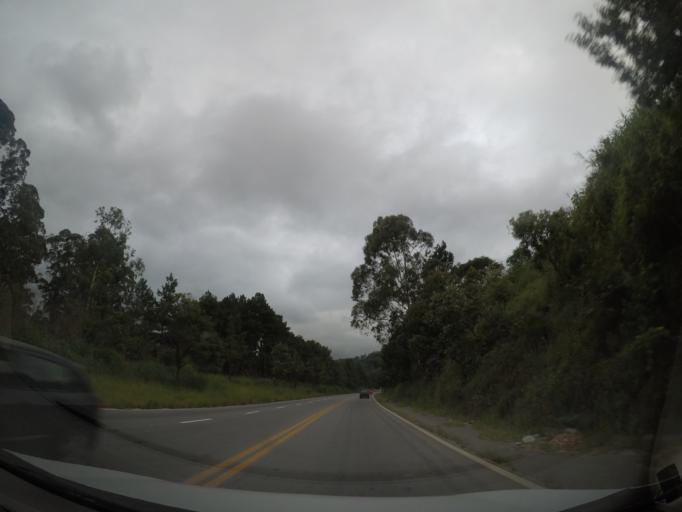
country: BR
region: Sao Paulo
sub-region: Aruja
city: Aruja
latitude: -23.3857
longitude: -46.4396
